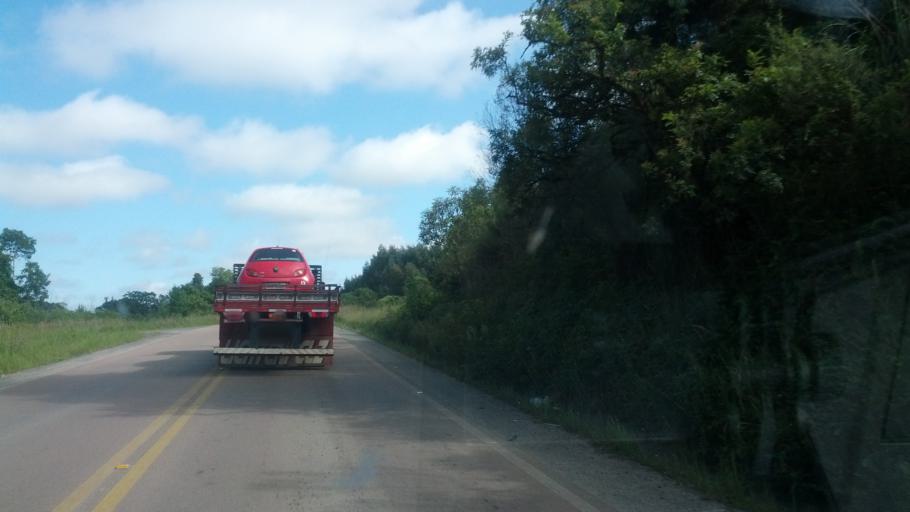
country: BR
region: Santa Catarina
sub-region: Otacilio Costa
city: Otacilio Costa
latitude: -27.4513
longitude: -50.1230
